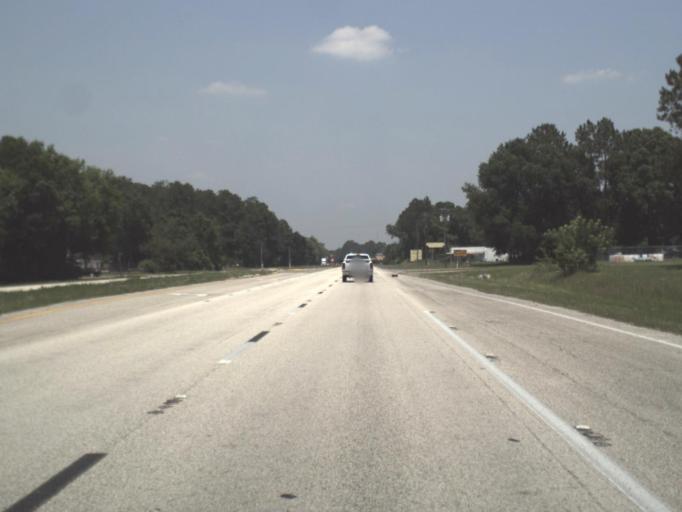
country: US
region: Florida
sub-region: Bradford County
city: Starke
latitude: 30.0258
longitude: -82.0817
